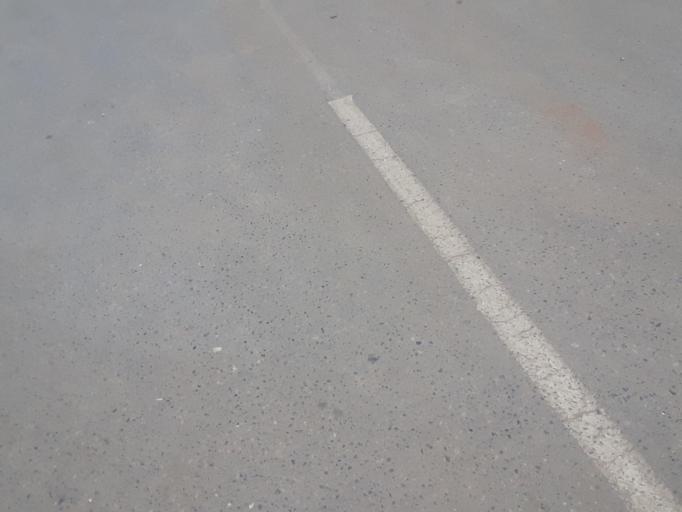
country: ZM
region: Lusaka
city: Lusaka
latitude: -15.3575
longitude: 28.2821
